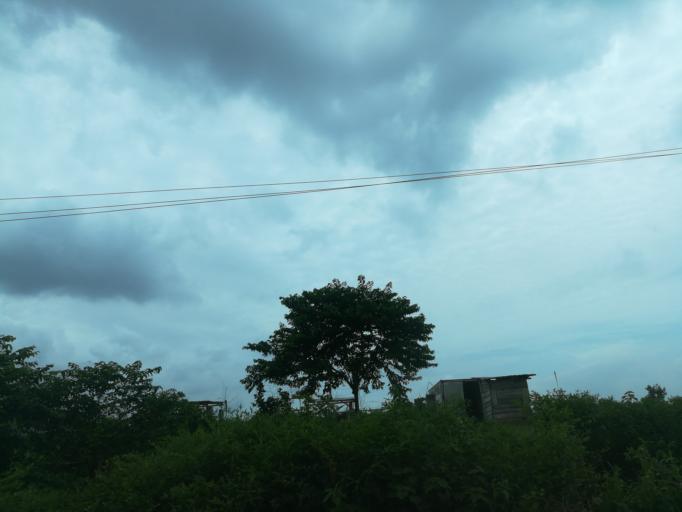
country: NG
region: Ogun
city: Odogbolu
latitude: 6.6559
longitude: 3.7122
